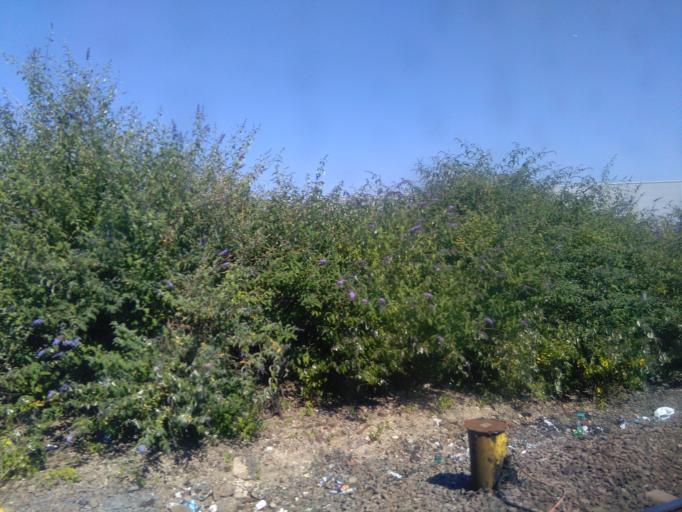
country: GB
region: England
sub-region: Luton
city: Luton
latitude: 51.8722
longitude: -0.3951
